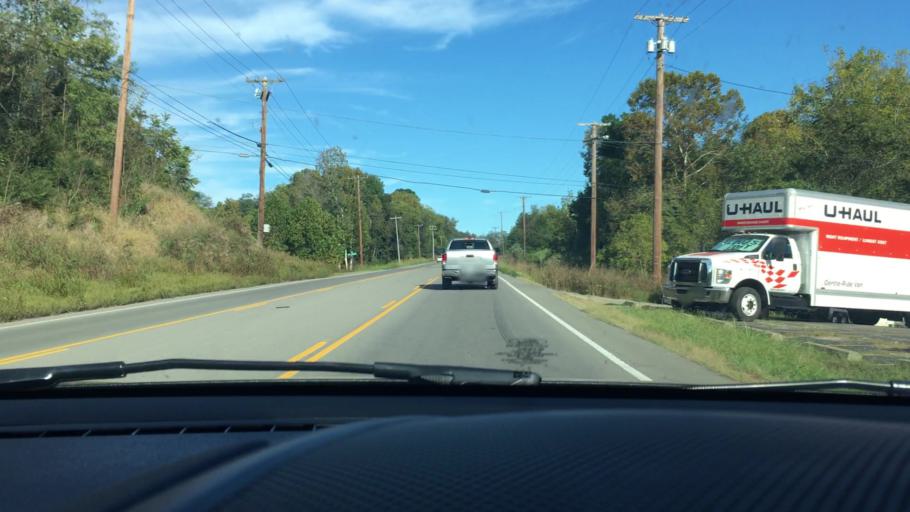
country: US
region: Tennessee
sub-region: Montgomery County
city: Clarksville
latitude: 36.5014
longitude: -87.3051
